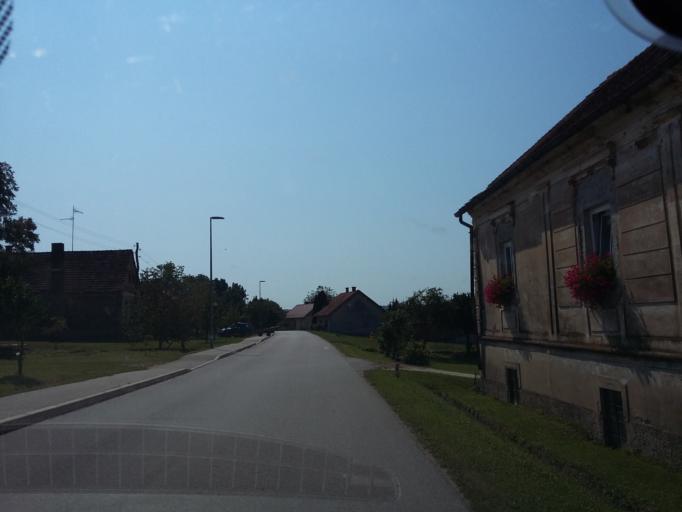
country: SI
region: Hodos-Hodos
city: Hodos
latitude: 46.8316
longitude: 16.3208
